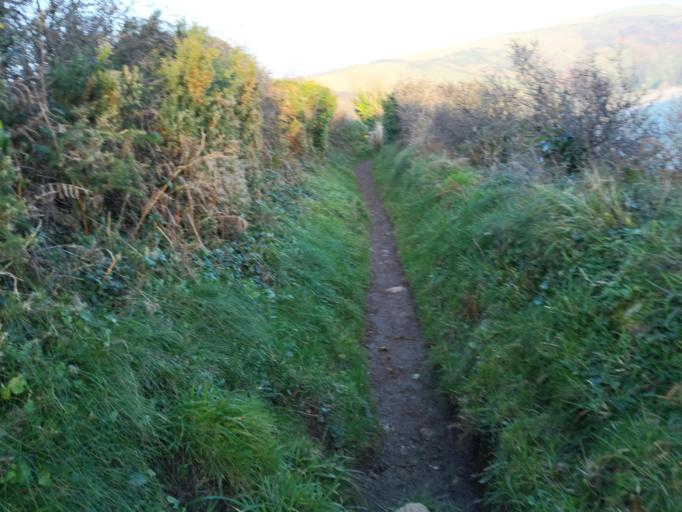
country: GB
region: England
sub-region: Cornwall
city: Fowey
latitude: 50.3264
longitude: -4.6163
